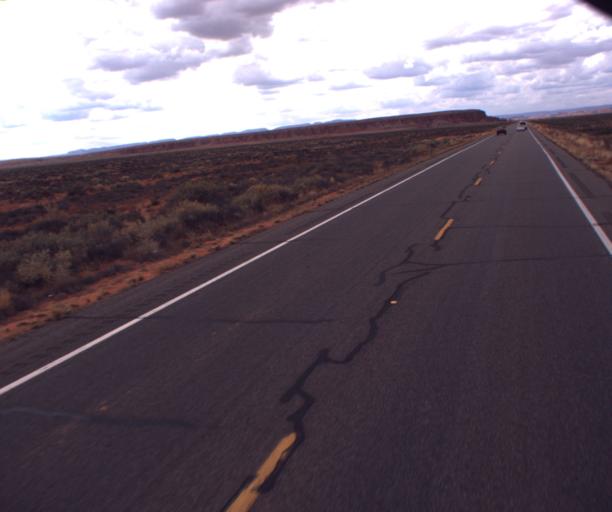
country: US
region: Arizona
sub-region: Navajo County
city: Kayenta
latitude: 36.7839
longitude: -109.9733
